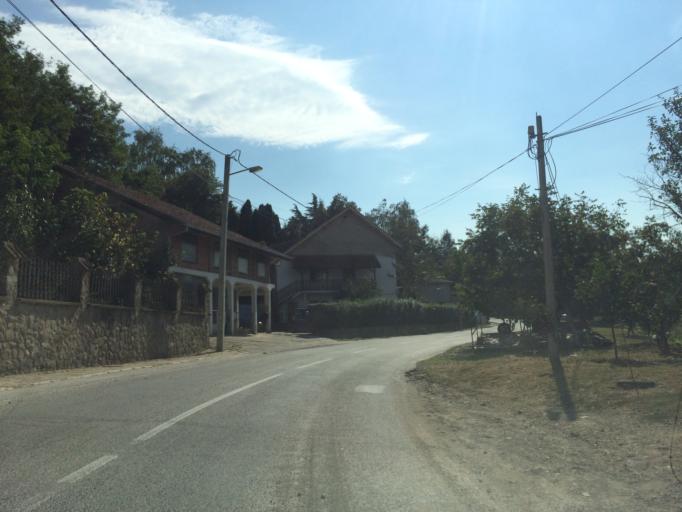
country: RS
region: Autonomna Pokrajina Vojvodina
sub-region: Juznobacki Okrug
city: Novi Sad
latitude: 45.2120
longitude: 19.8083
